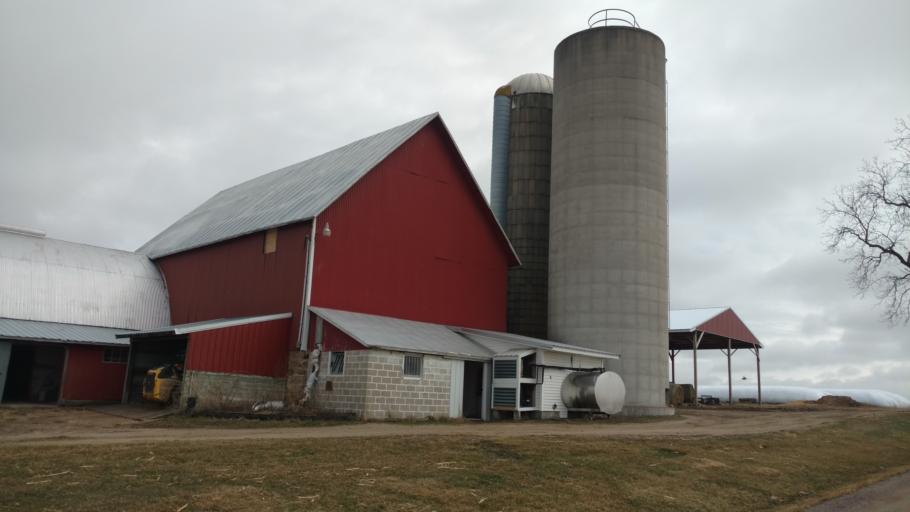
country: US
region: Wisconsin
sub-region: Vernon County
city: Hillsboro
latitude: 43.6005
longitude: -90.3236
